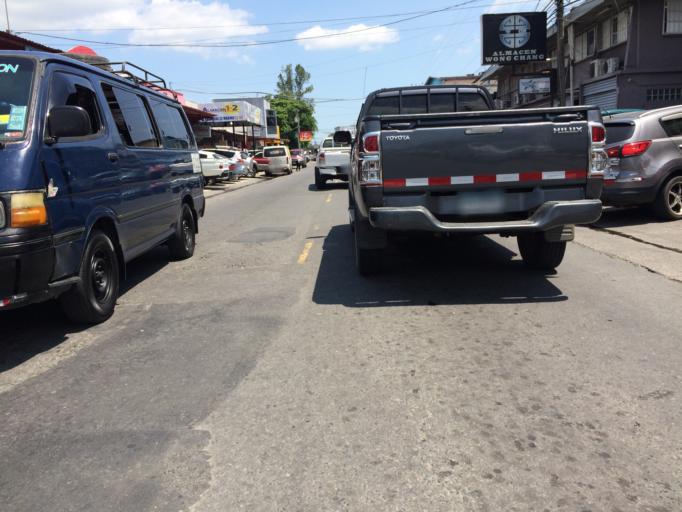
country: CR
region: Puntarenas
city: Canoas
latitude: 8.5324
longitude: -82.8378
